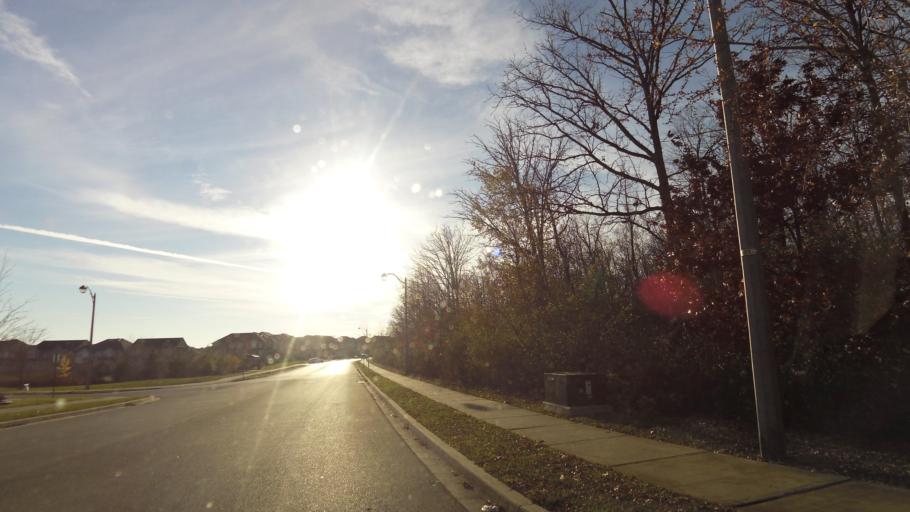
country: CA
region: Ontario
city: Brampton
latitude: 43.7905
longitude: -79.7451
